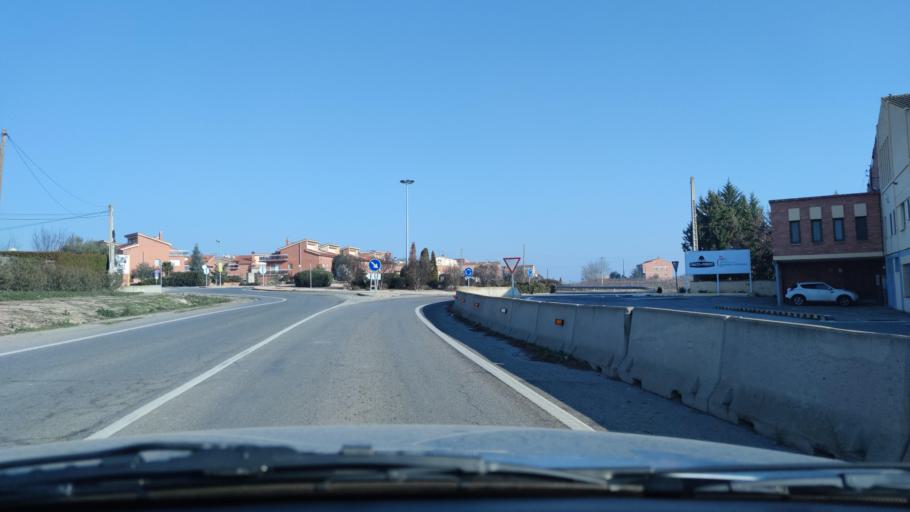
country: ES
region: Catalonia
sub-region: Provincia de Lleida
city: Torrefarrera
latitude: 41.6901
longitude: 0.6332
